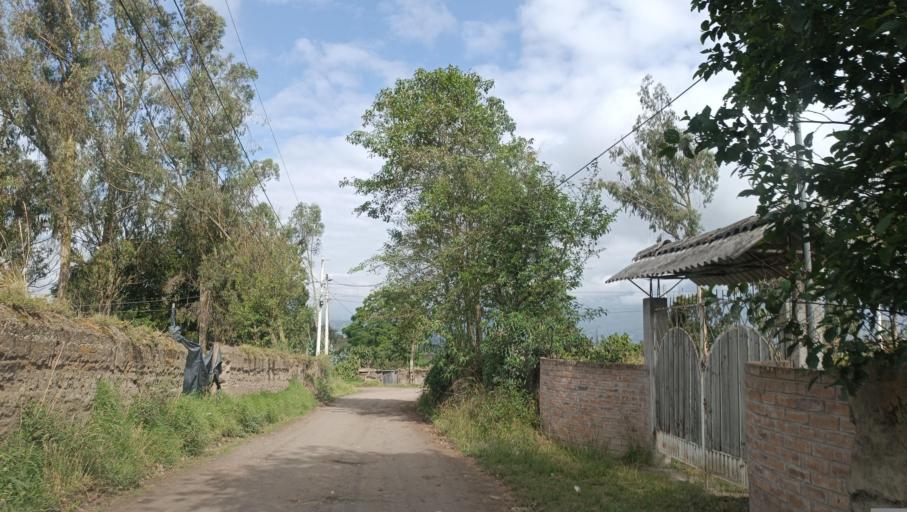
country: EC
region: Chimborazo
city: Guano
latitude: -1.6552
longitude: -78.5679
